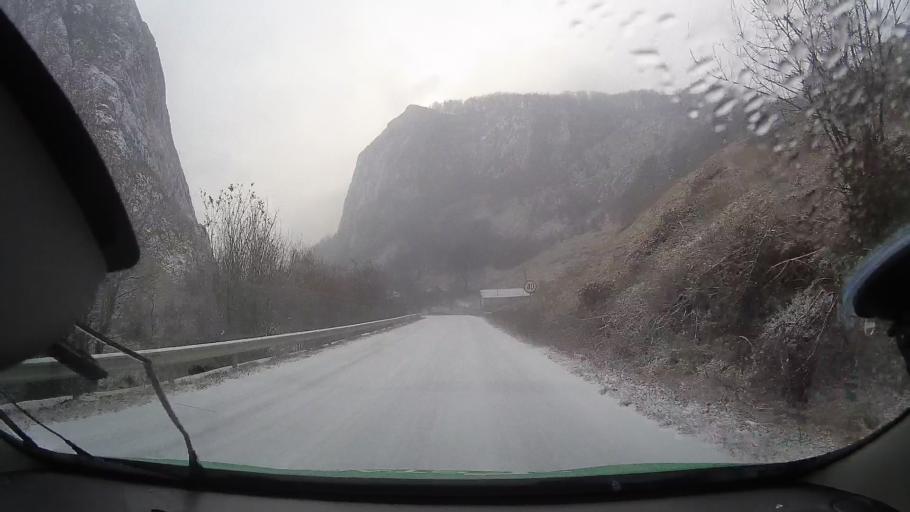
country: RO
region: Alba
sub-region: Comuna Livezile
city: Livezile
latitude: 46.3765
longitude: 23.5828
